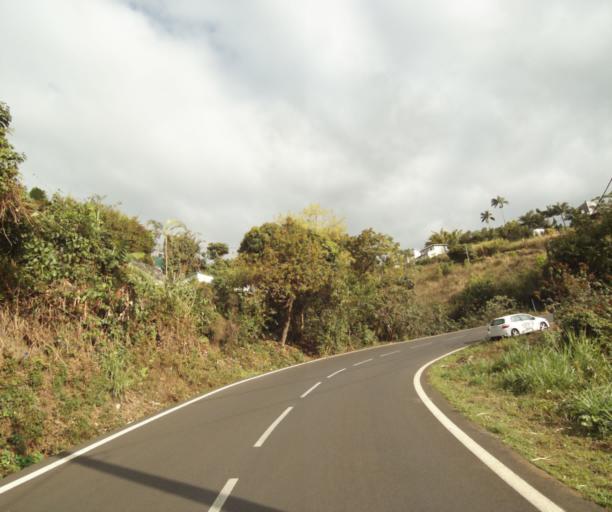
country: RE
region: Reunion
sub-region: Reunion
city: Saint-Paul
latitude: -21.0300
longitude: 55.3115
